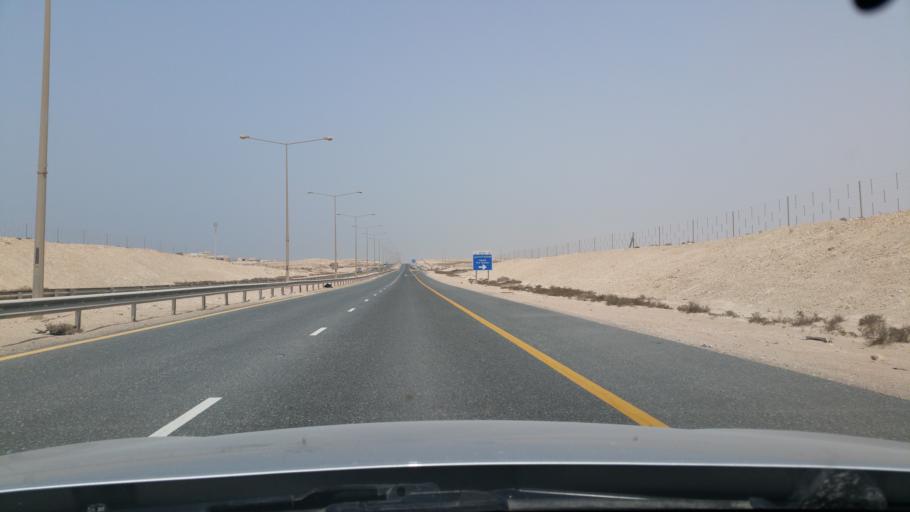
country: QA
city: Umm Bab
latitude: 25.3191
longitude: 50.7897
